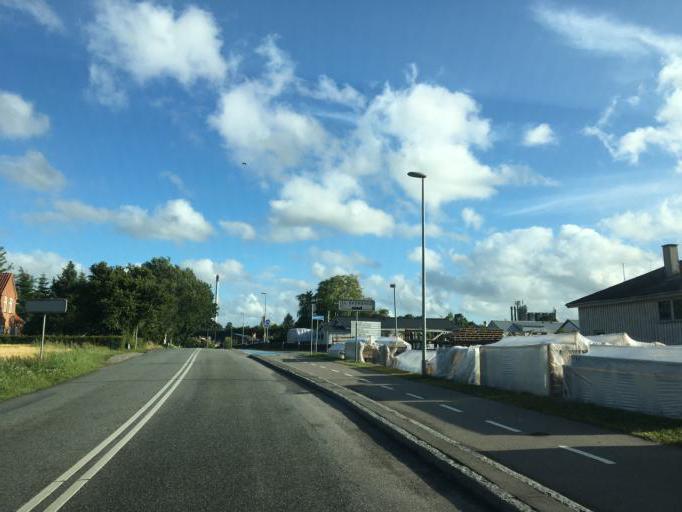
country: DK
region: Zealand
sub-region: Solrod Kommune
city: Havdrup
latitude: 55.5133
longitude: 12.1442
